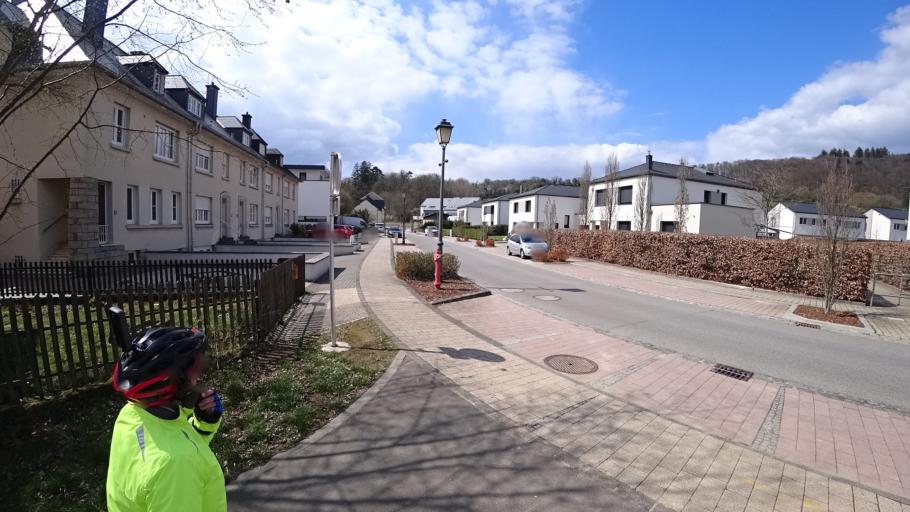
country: LU
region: Luxembourg
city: Colmar
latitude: 49.8177
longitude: 6.0933
